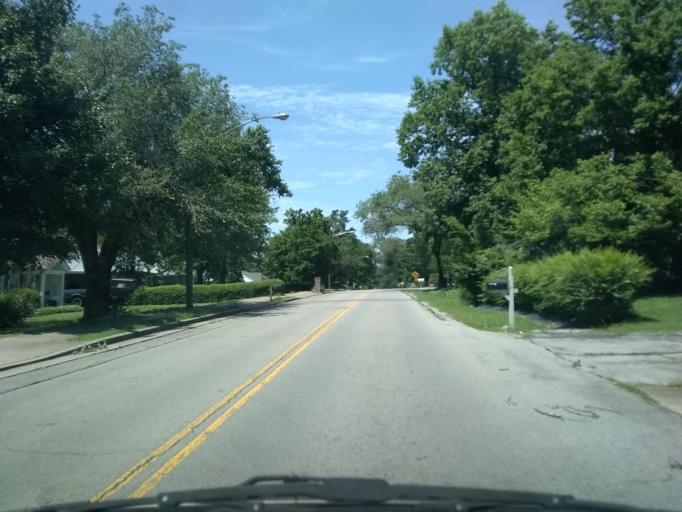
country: US
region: Tennessee
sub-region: Davidson County
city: Nashville
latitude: 36.1285
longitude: -86.7004
